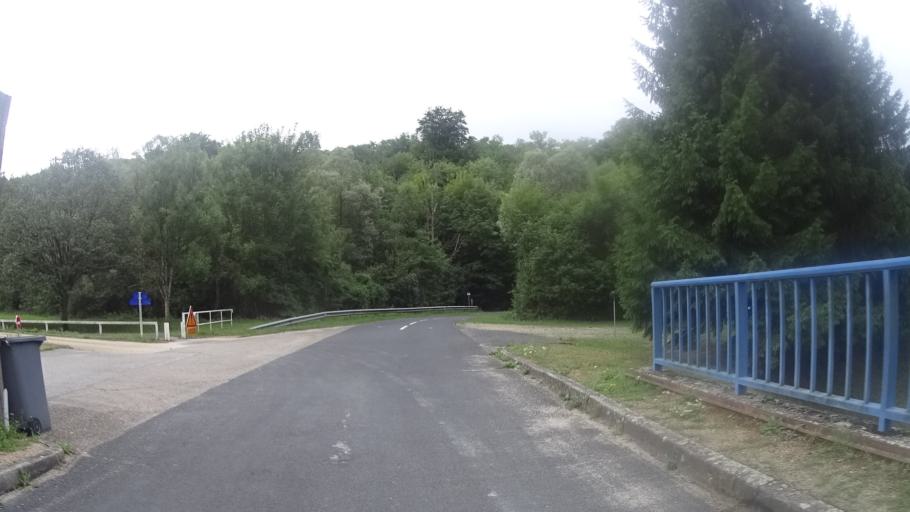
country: FR
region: Lorraine
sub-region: Departement de Meurthe-et-Moselle
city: Gondreville
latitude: 48.6493
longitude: 5.9740
